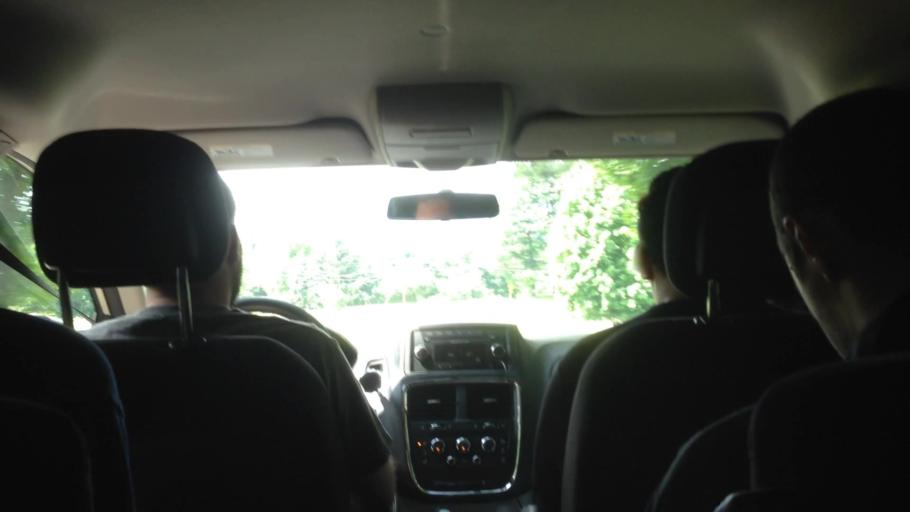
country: US
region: New York
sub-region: Dutchess County
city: Tivoli
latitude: 42.0550
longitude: -73.8899
